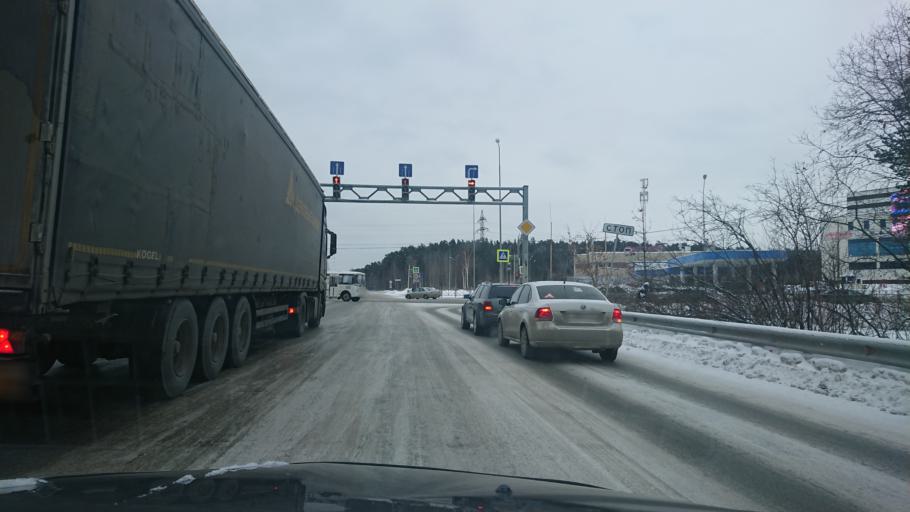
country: RU
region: Sverdlovsk
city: Shirokaya Rechka
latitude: 56.8133
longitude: 60.5164
